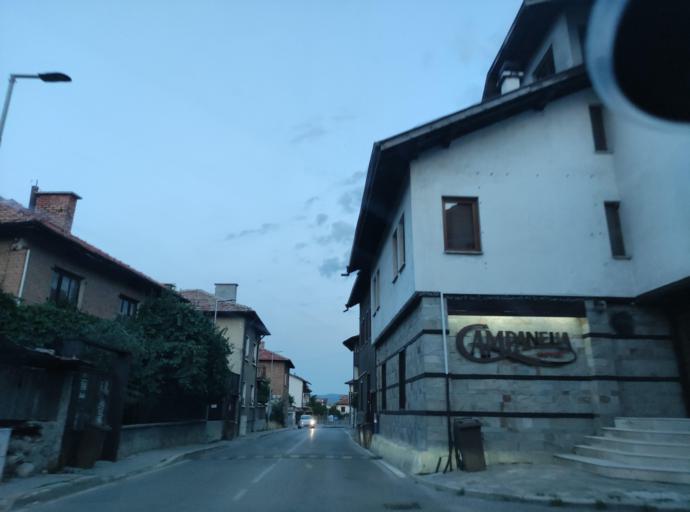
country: BG
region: Blagoevgrad
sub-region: Obshtina Bansko
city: Bansko
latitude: 41.8335
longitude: 23.4883
